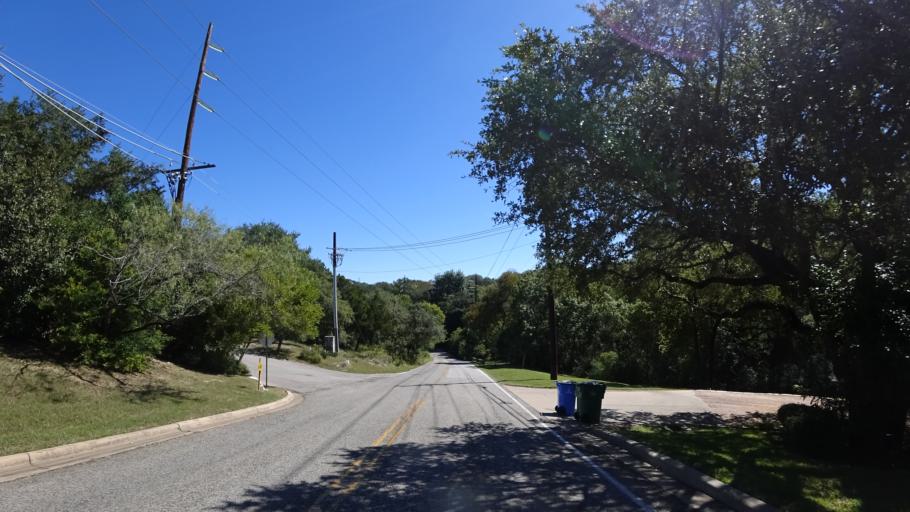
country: US
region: Texas
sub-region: Travis County
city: West Lake Hills
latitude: 30.3280
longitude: -97.7837
